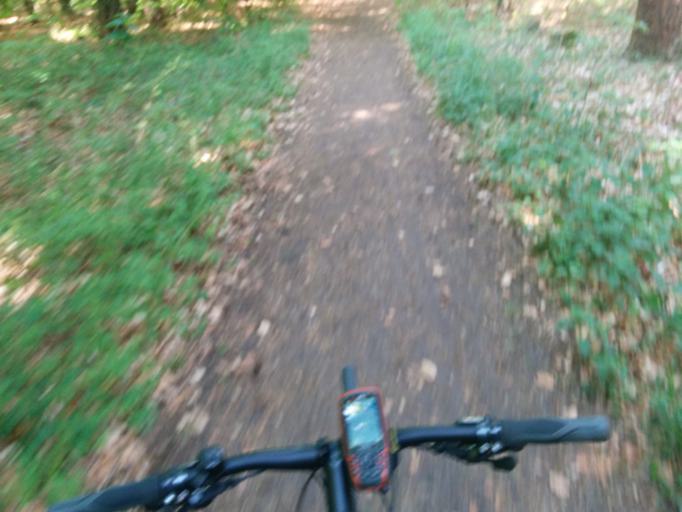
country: DE
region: Mecklenburg-Vorpommern
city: Ostseebad Zinnowitz
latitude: 54.0717
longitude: 13.9376
